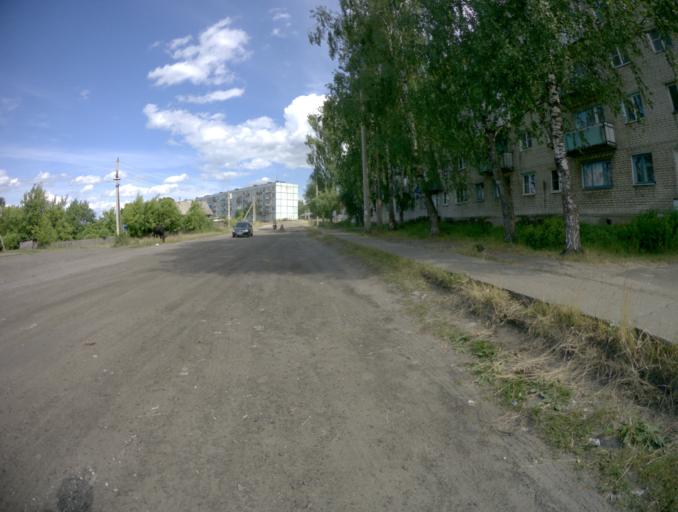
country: RU
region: Nizjnij Novgorod
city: Frolishchi
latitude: 56.4239
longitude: 42.6481
